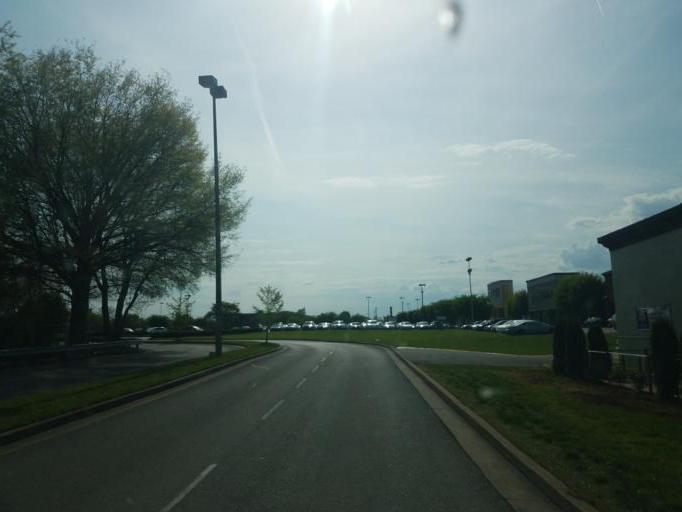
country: US
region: Kentucky
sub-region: Warren County
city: Bowling Green
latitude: 36.9521
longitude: -86.4273
